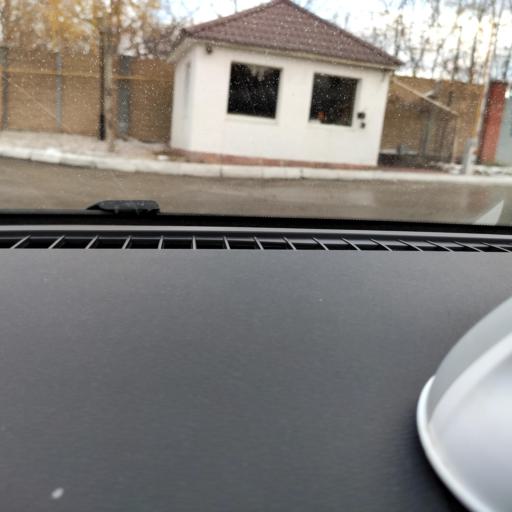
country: RU
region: Samara
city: Samara
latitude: 53.2390
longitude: 50.1735
